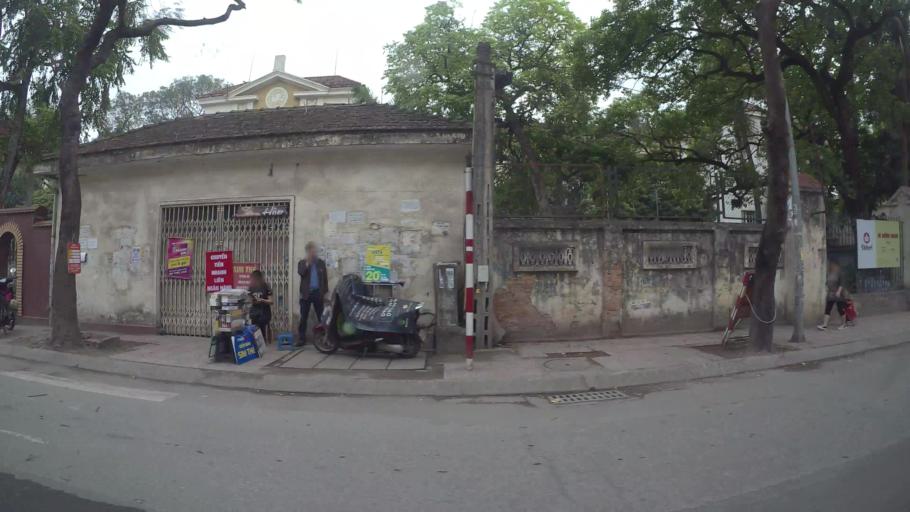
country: VN
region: Ha Noi
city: Cau Giay
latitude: 21.0354
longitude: 105.8194
